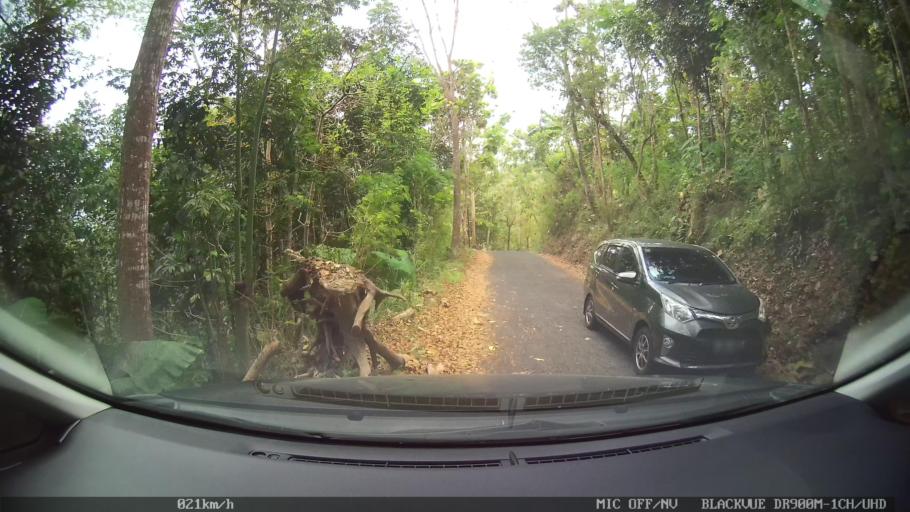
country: ID
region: Central Java
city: Candi Prambanan
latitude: -7.8016
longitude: 110.5209
